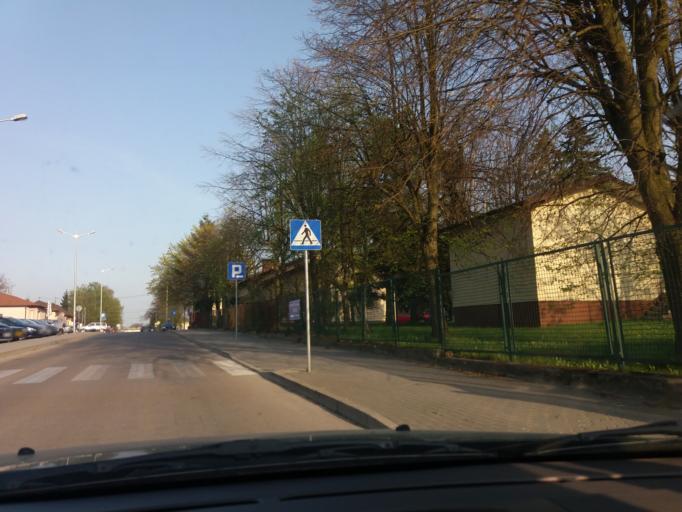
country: PL
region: Masovian Voivodeship
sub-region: Powiat mlawski
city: Mlawa
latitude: 53.1240
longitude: 20.3707
